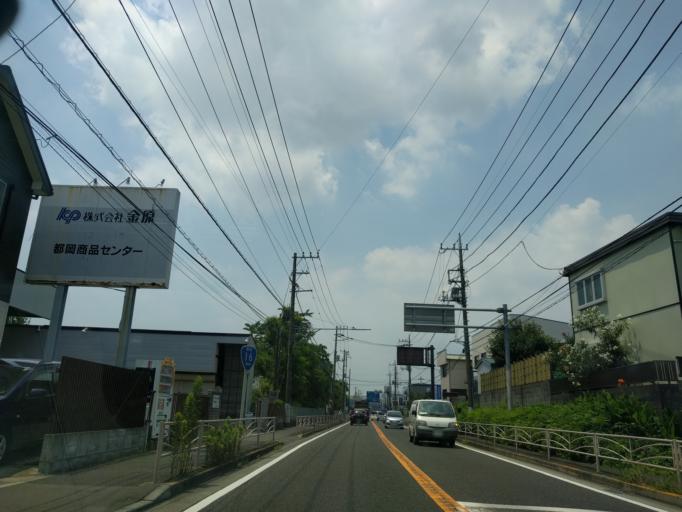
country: JP
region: Kanagawa
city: Minami-rinkan
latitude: 35.4850
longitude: 139.5228
